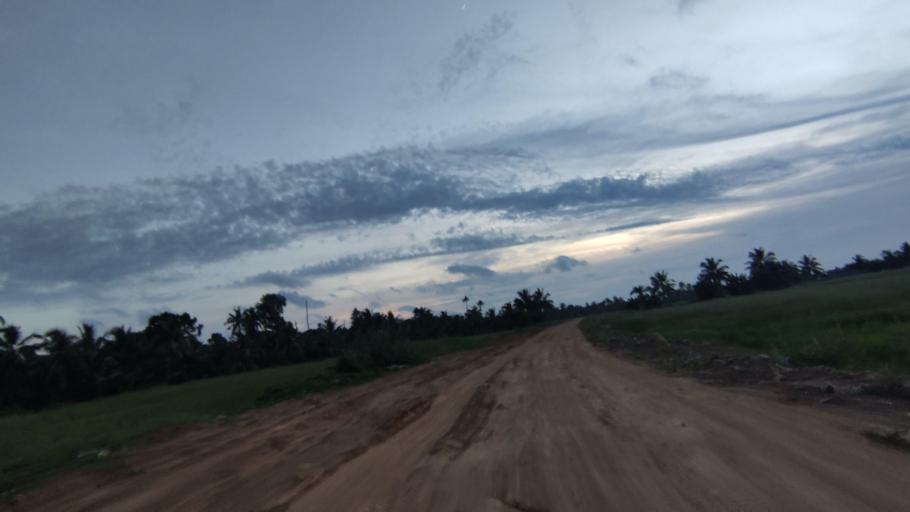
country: IN
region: Kerala
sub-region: Kottayam
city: Kottayam
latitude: 9.6454
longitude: 76.4575
